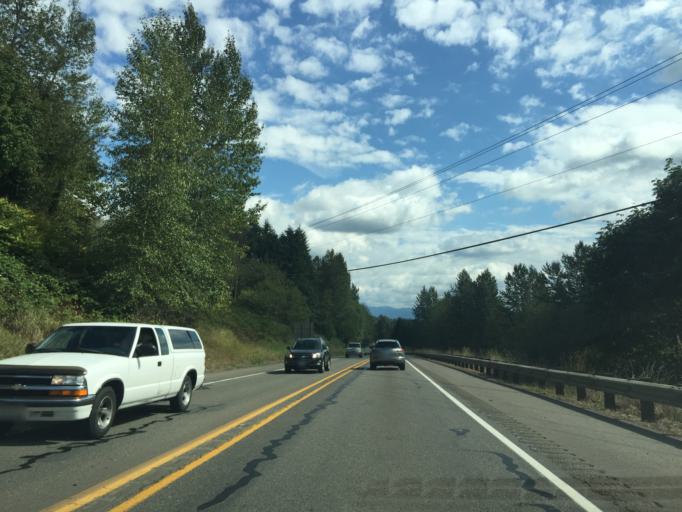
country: US
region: Washington
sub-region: Snohomish County
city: Snohomish
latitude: 47.9133
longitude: -122.0623
